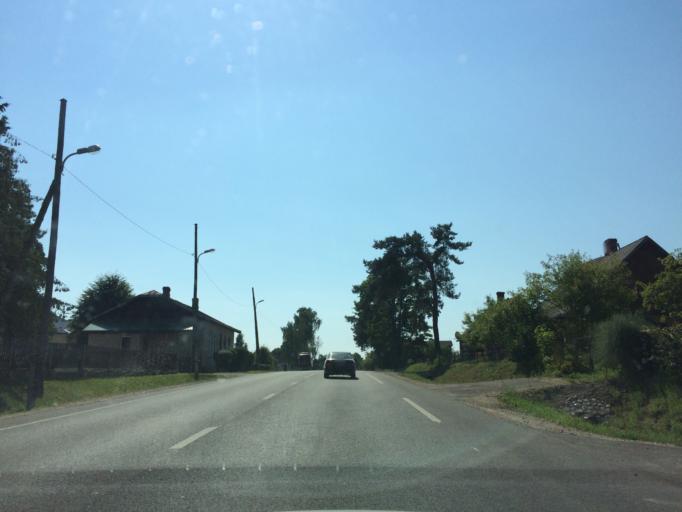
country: LV
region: Rezekne
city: Rezekne
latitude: 56.3489
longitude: 27.1677
